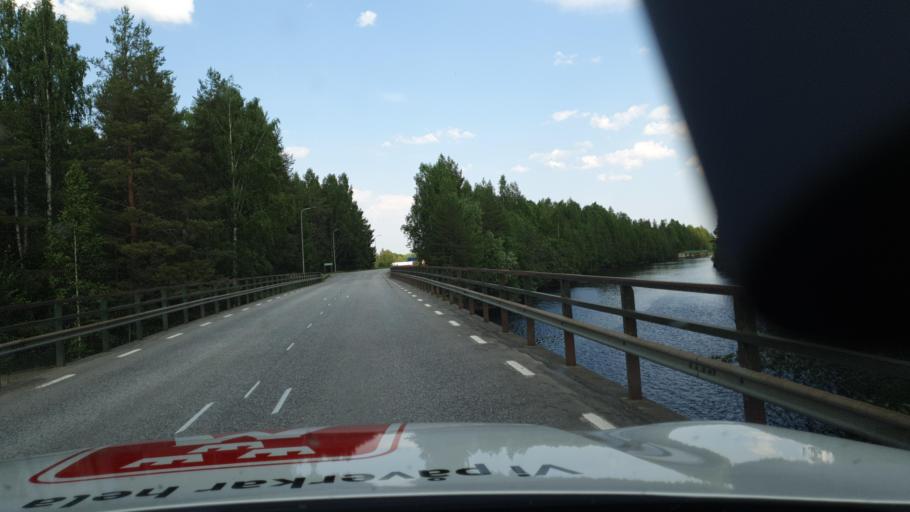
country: SE
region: Vaesterbotten
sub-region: Skelleftea Kommun
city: Viken
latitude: 64.7391
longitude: 20.7685
